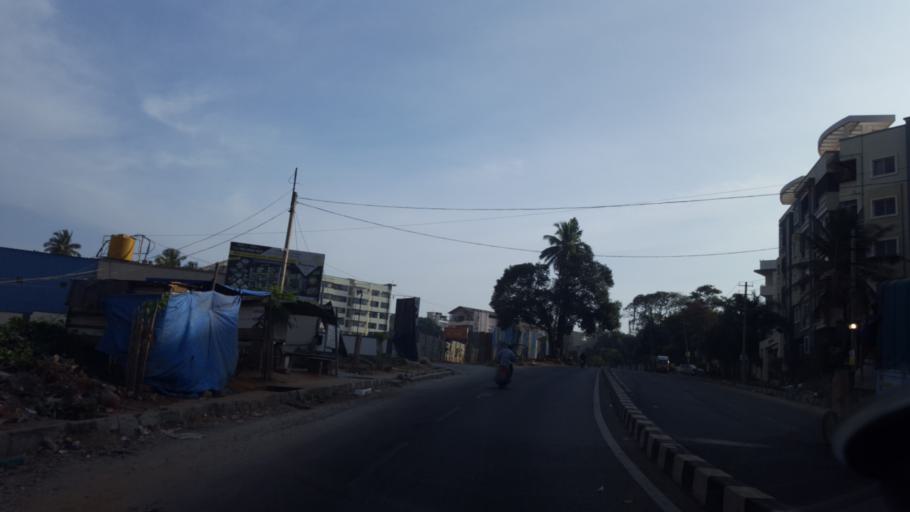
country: IN
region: Karnataka
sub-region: Bangalore Urban
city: Bangalore
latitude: 12.9085
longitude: 77.5122
